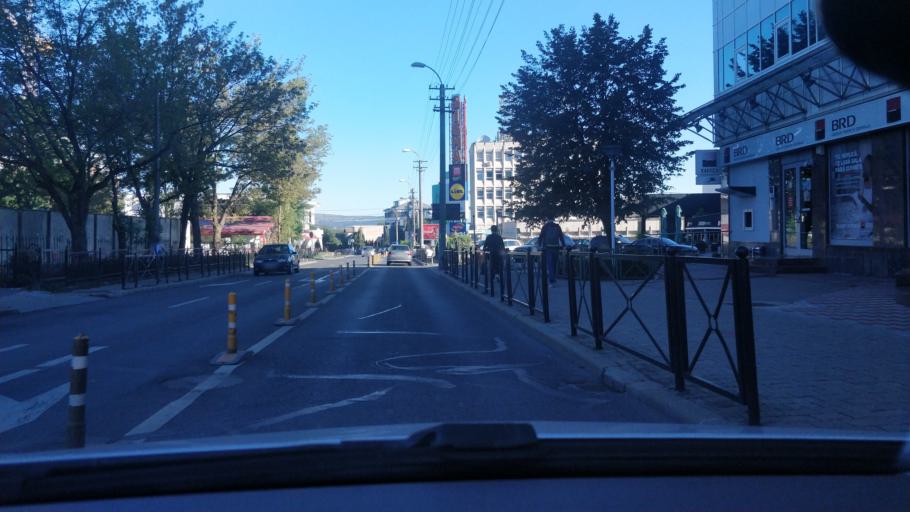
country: RO
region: Cluj
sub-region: Municipiul Cluj-Napoca
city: Cluj-Napoca
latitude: 46.7562
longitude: 23.5943
